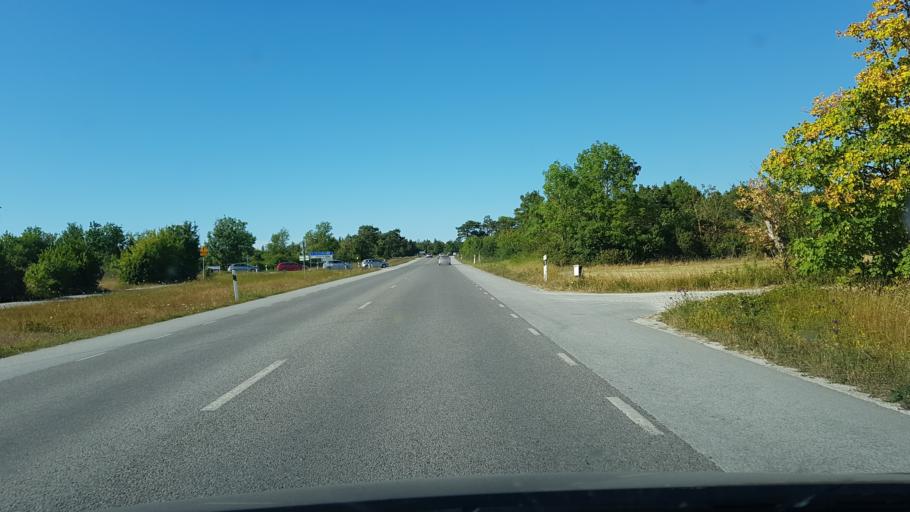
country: SE
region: Gotland
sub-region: Gotland
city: Klintehamn
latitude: 57.5015
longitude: 18.1524
